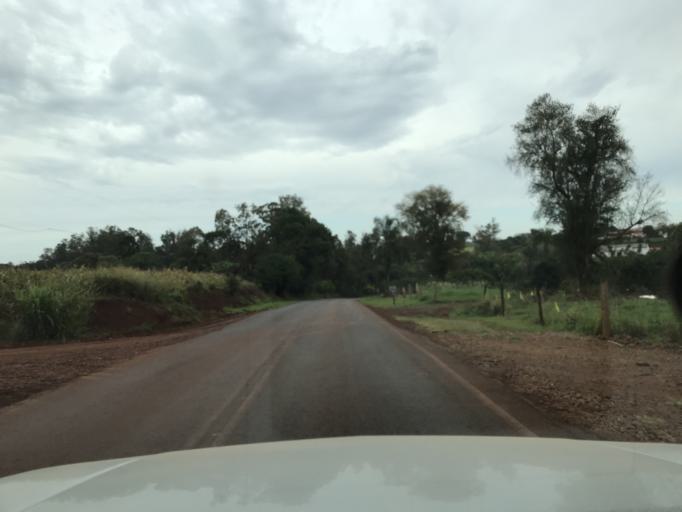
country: BR
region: Parana
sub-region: Marechal Candido Rondon
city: Marechal Candido Rondon
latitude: -24.4546
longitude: -53.9340
